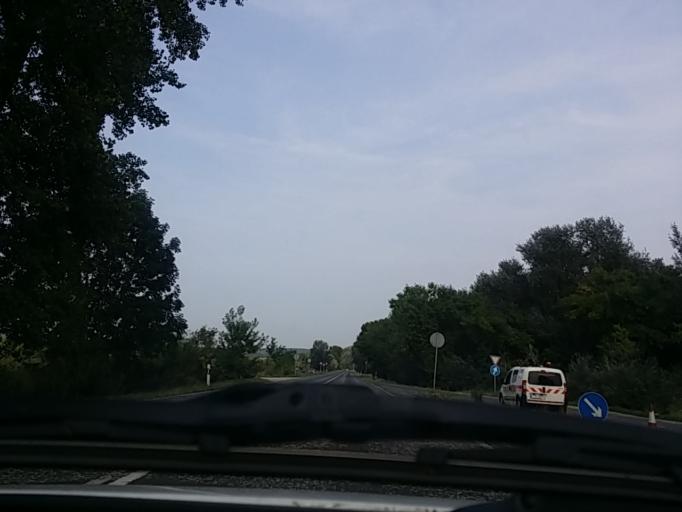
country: HU
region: Pest
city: Biatorbagy
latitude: 47.4893
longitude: 18.8019
